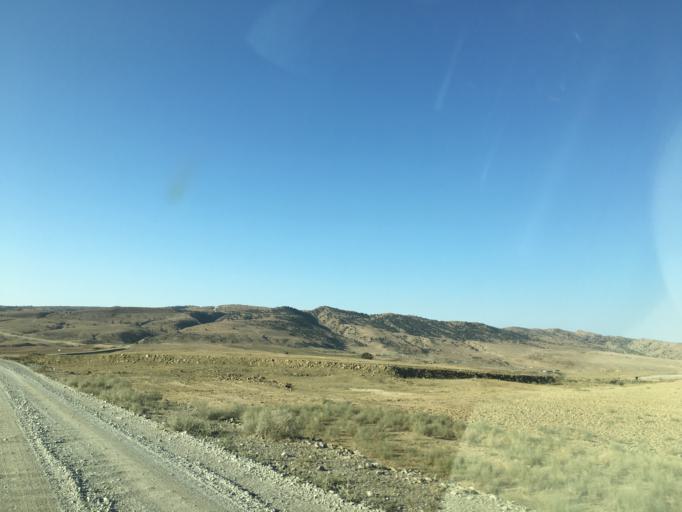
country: TM
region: Ahal
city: Baharly
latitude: 38.3863
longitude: 56.9768
